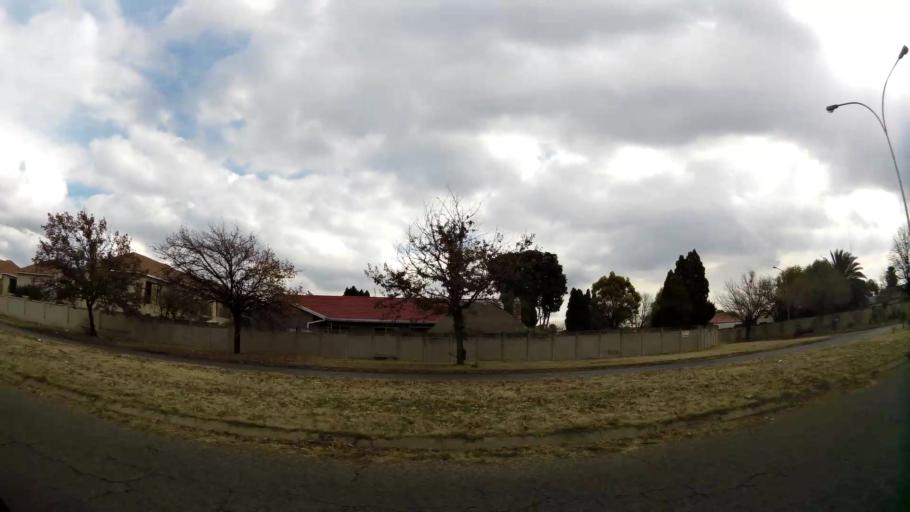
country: ZA
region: Gauteng
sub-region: Sedibeng District Municipality
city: Vanderbijlpark
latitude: -26.7293
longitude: 27.8534
